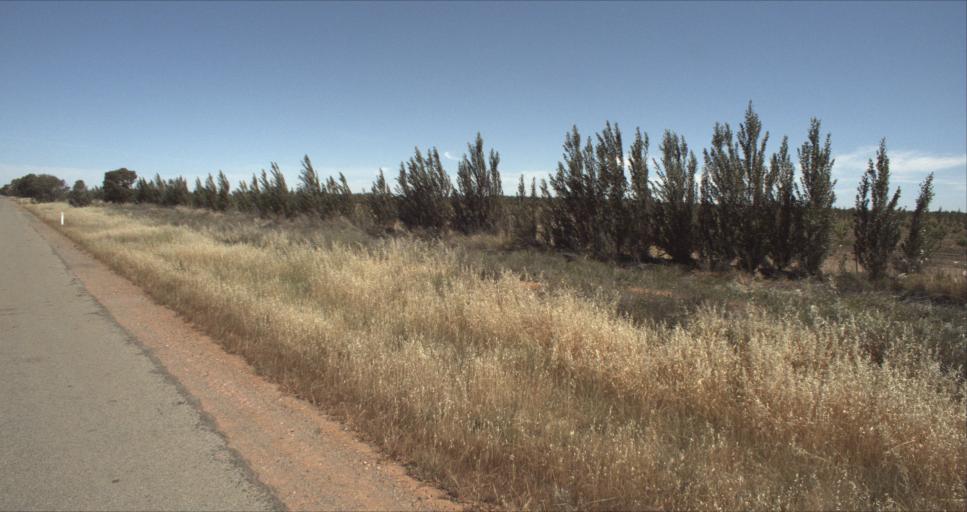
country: AU
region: New South Wales
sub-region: Leeton
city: Leeton
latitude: -34.5139
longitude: 146.3451
